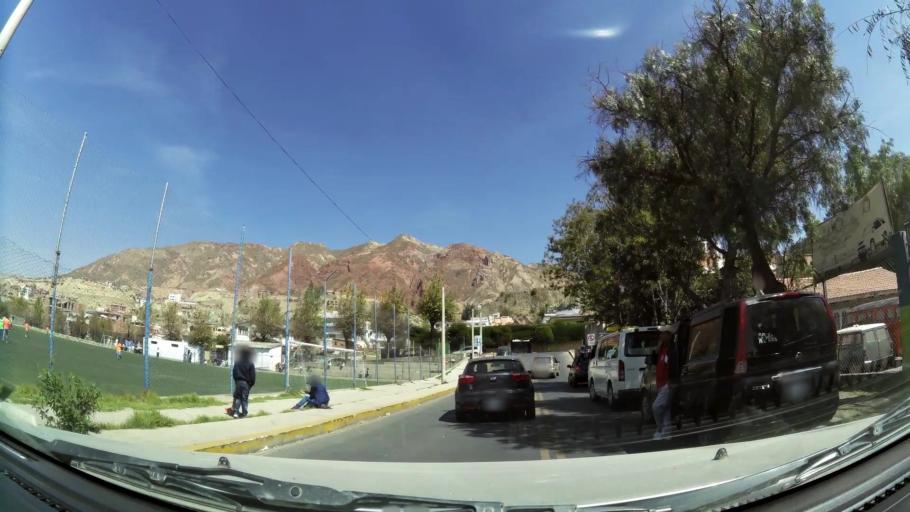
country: BO
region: La Paz
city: La Paz
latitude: -16.5423
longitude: -68.0946
